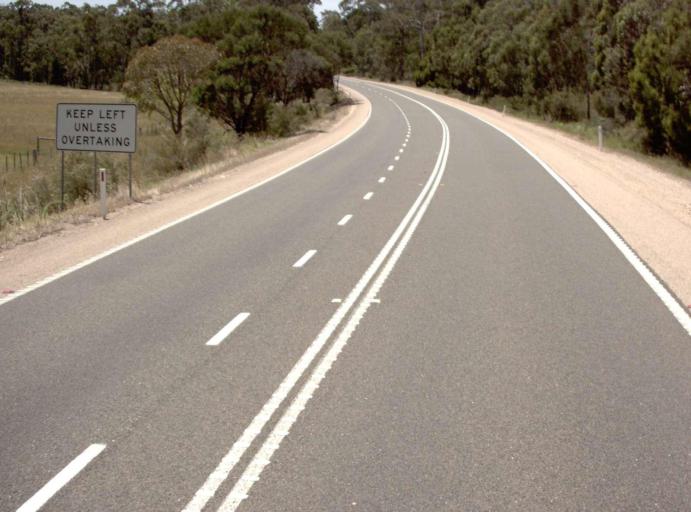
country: AU
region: Victoria
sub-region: East Gippsland
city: Bairnsdale
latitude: -37.7454
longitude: 147.7603
